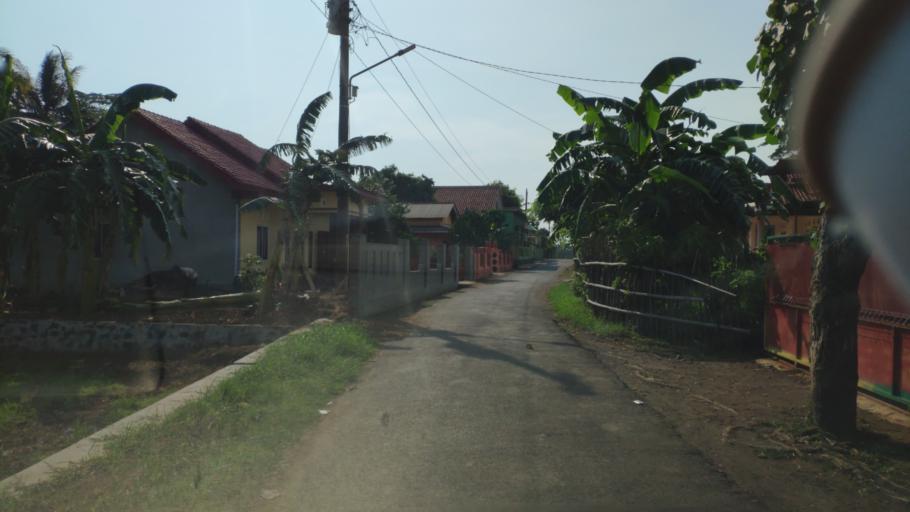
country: ID
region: Central Java
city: Karangbadar Kidul
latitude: -7.6974
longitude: 108.9867
